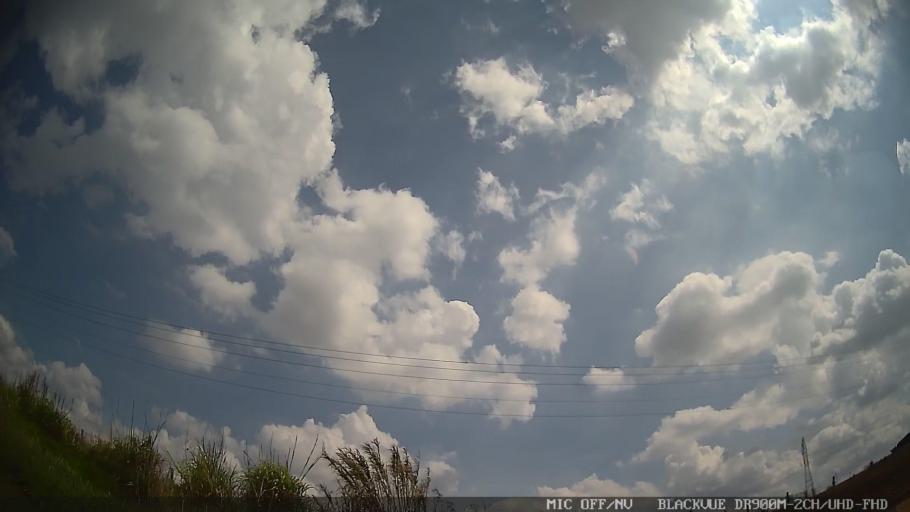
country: BR
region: Sao Paulo
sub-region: Braganca Paulista
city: Braganca Paulista
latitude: -22.9444
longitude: -46.6748
